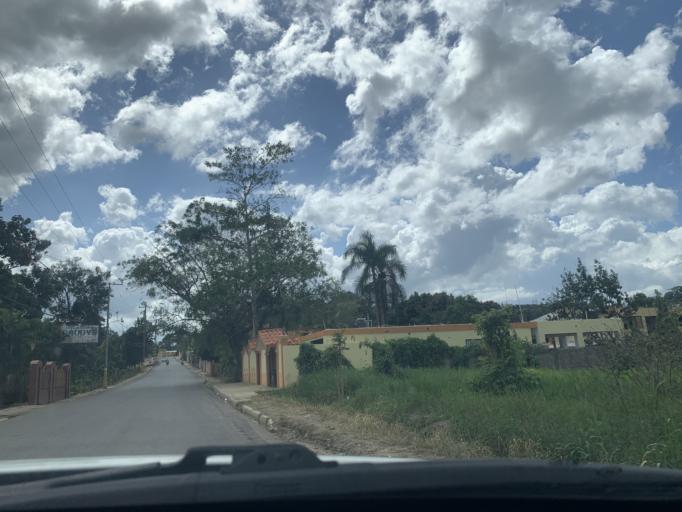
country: DO
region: Monte Plata
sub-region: Yamasa
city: Yamasa
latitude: 18.7806
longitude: -70.0242
